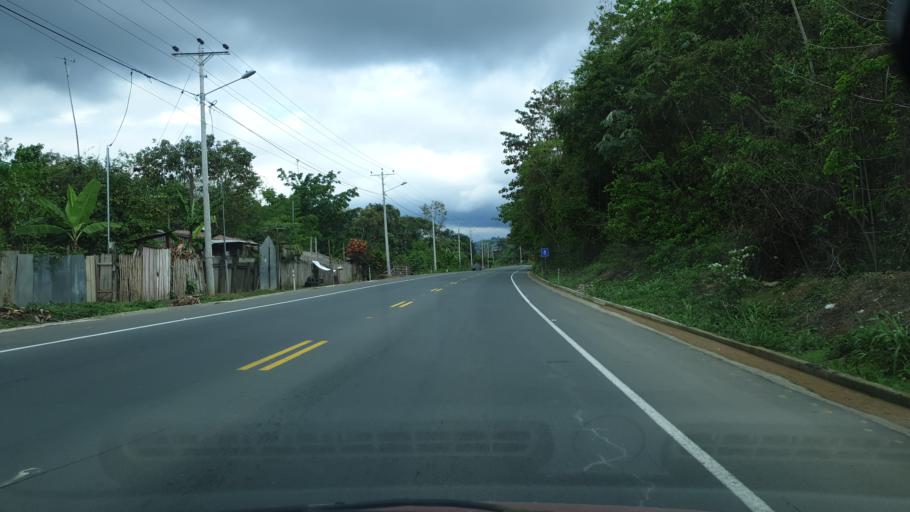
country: EC
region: Manabi
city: Pajan
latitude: -1.5597
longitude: -80.5252
